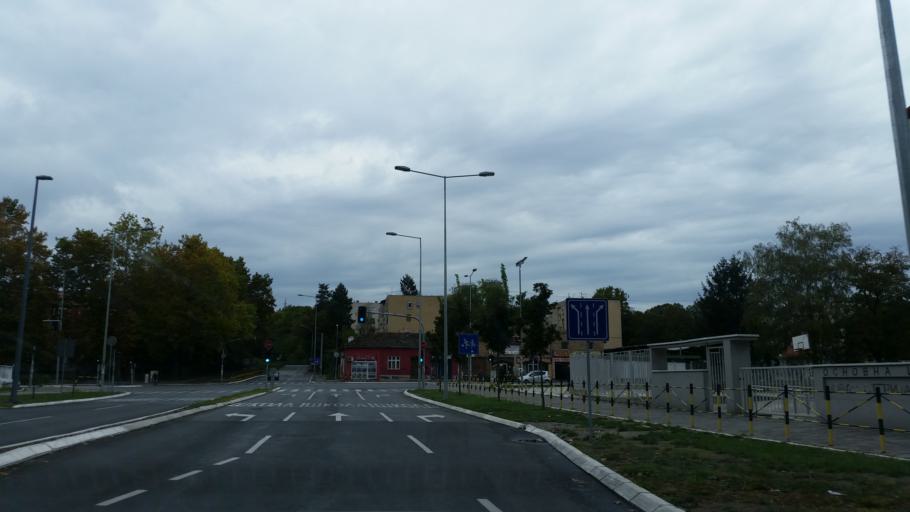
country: RS
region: Central Serbia
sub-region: Belgrade
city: Zemun
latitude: 44.8072
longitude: 20.3769
